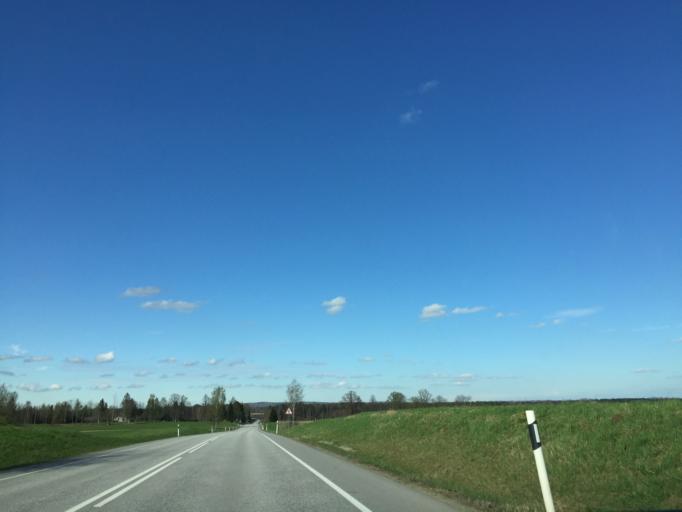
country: EE
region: Vorumaa
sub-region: Antsla vald
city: Vana-Antsla
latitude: 57.8810
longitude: 26.2813
